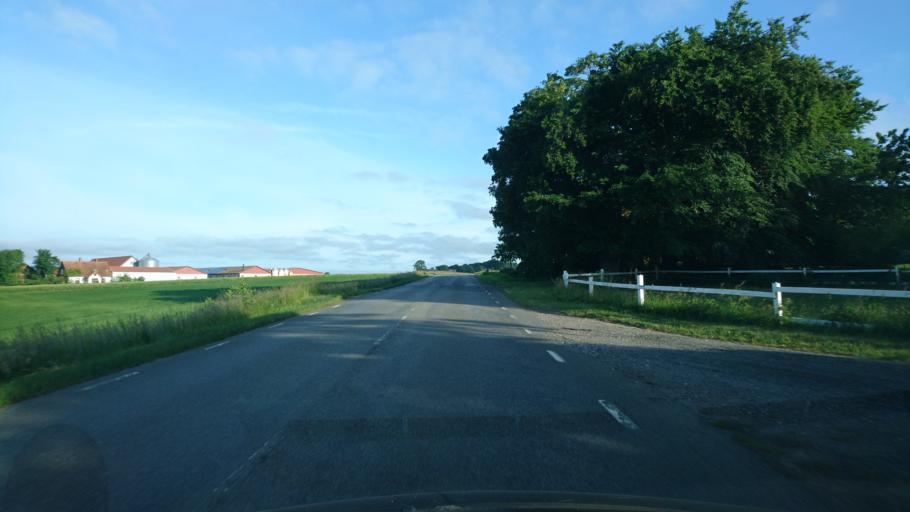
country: SE
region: Skane
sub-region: Tomelilla Kommun
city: Tomelilla
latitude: 55.4621
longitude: 14.1019
